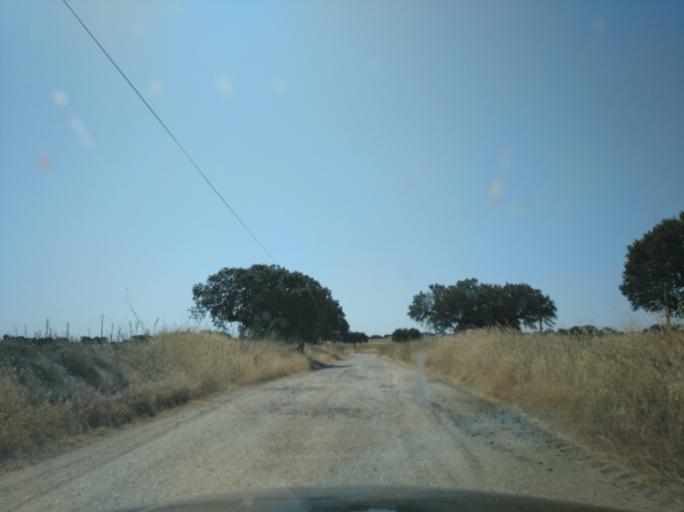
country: PT
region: Portalegre
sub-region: Campo Maior
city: Campo Maior
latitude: 39.0338
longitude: -6.9836
